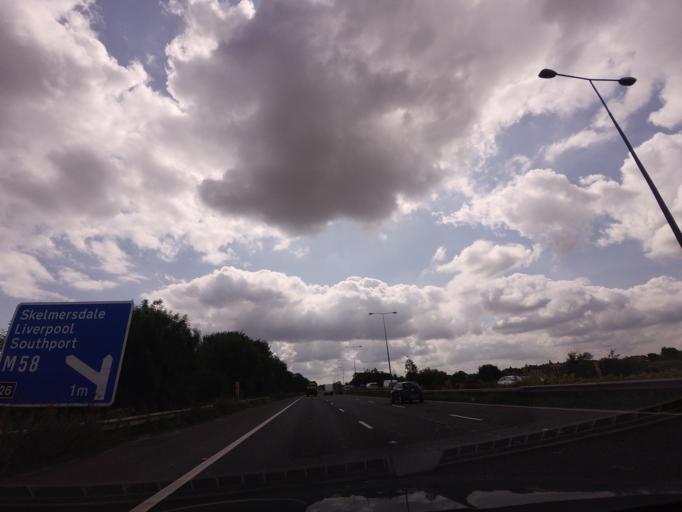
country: GB
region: England
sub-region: Borough of Wigan
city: Shevington
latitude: 53.5501
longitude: -2.7003
